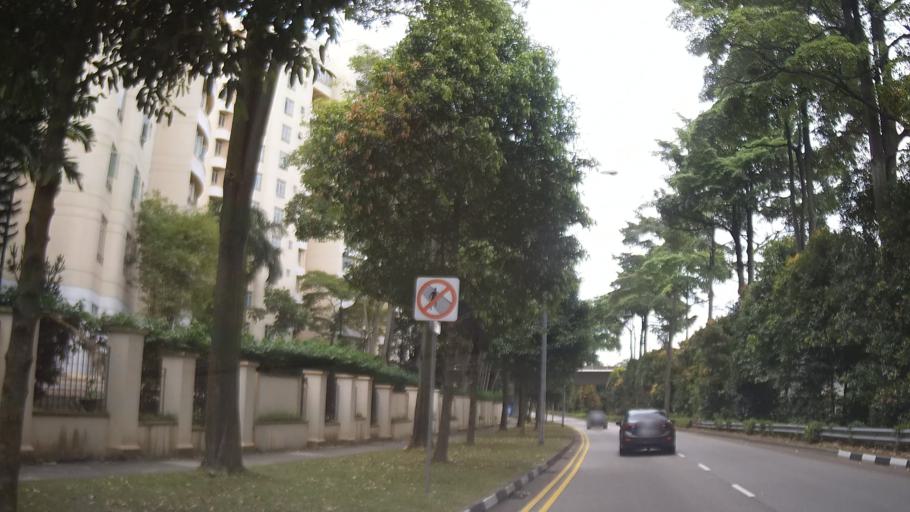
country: MY
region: Johor
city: Johor Bahru
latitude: 1.3887
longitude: 103.7452
